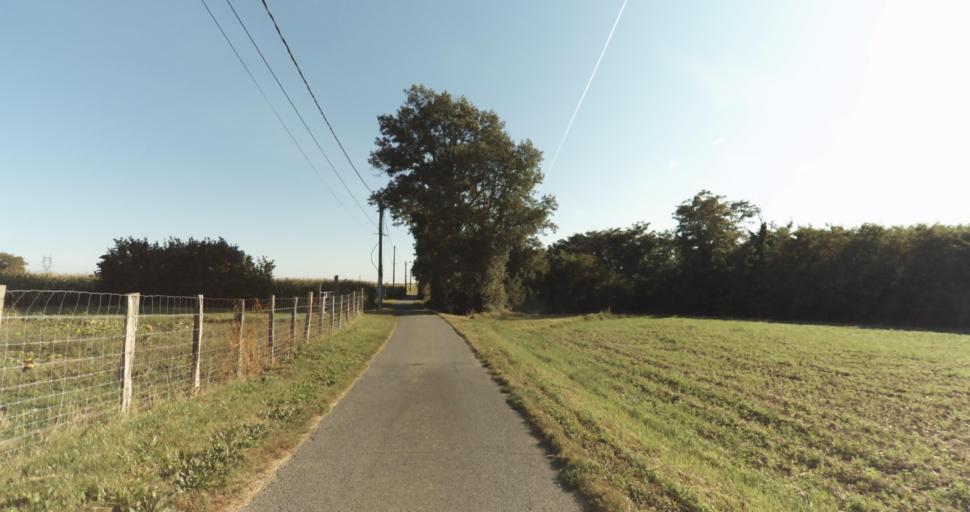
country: FR
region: Rhone-Alpes
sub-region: Departement du Rhone
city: Montanay
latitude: 45.8955
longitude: 4.8582
